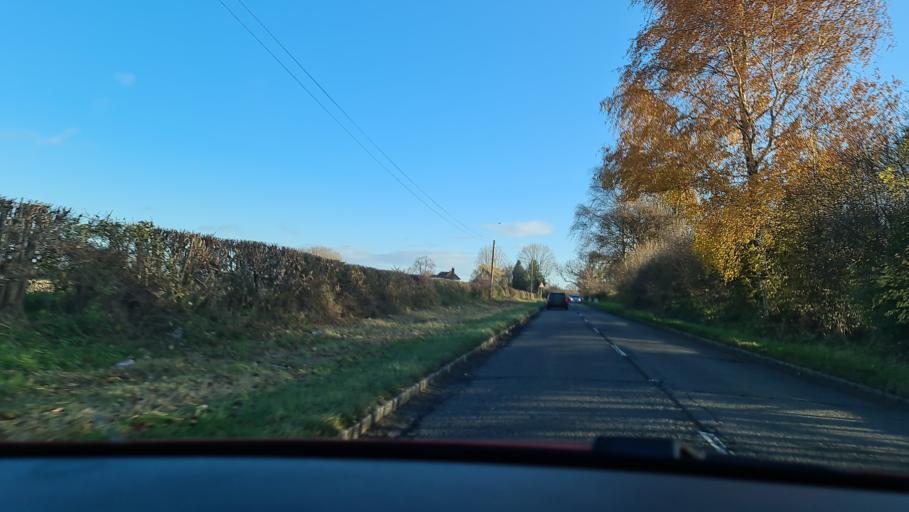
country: GB
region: England
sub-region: Buckinghamshire
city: Weston Turville
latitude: 51.7696
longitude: -0.7769
